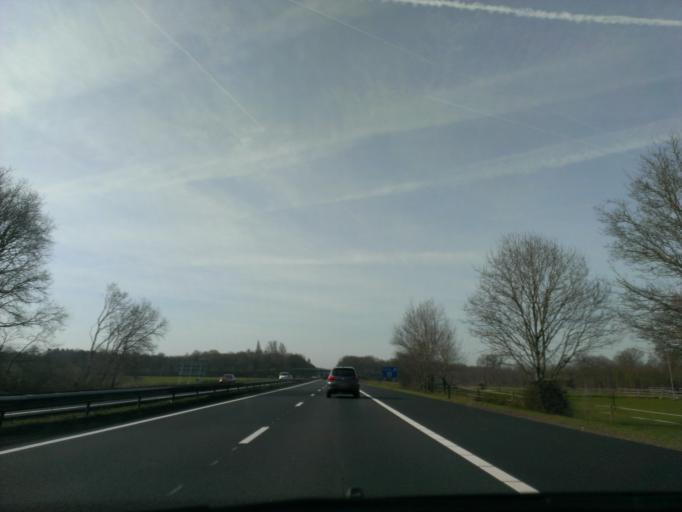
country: NL
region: Gelderland
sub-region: Gemeente Oldebroek
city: Oldebroek
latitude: 52.4610
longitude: 5.9818
